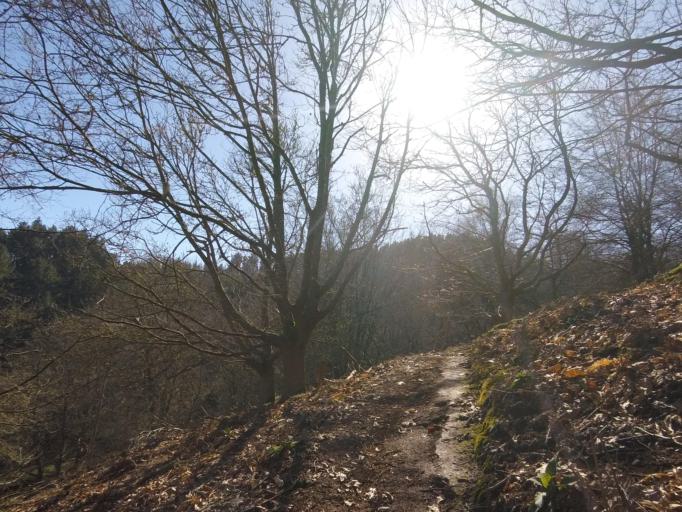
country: PT
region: Madeira
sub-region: Funchal
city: Nossa Senhora do Monte
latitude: 32.6990
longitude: -16.8799
